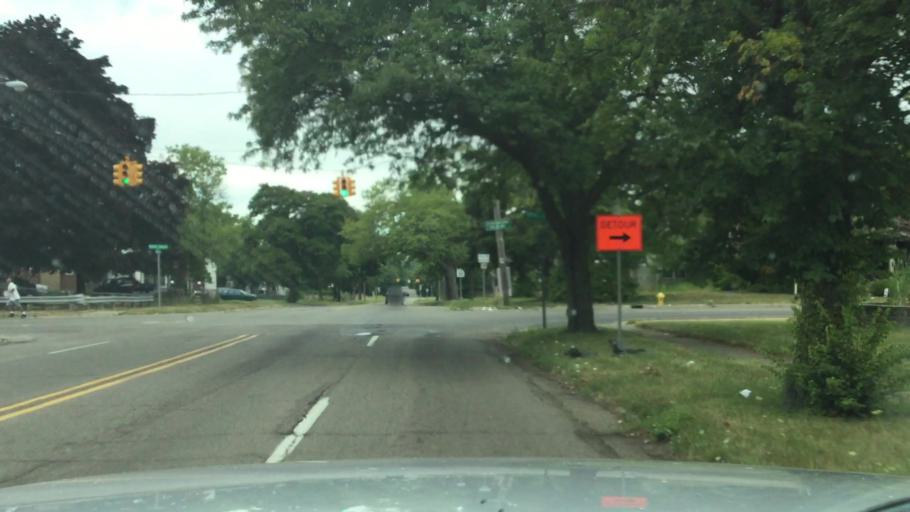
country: US
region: Michigan
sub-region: Genesee County
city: Flint
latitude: 43.0362
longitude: -83.7041
